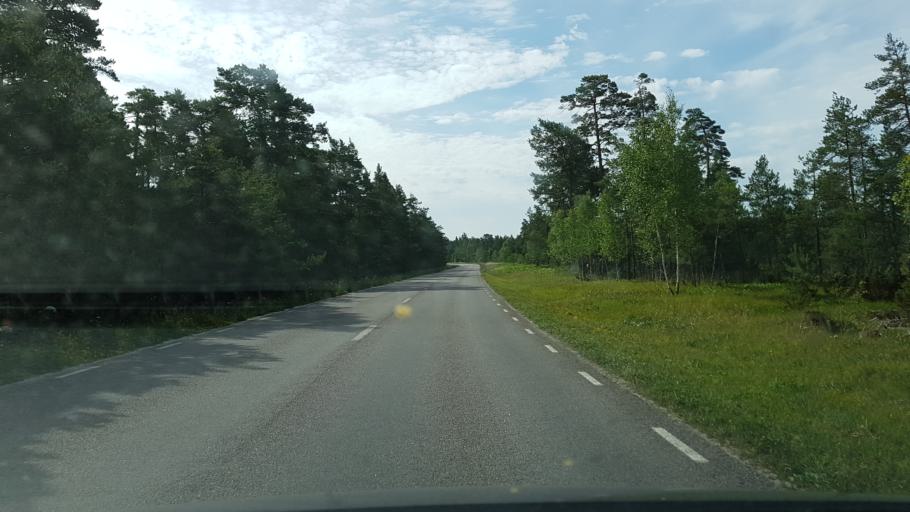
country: SE
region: Gotland
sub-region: Gotland
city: Hemse
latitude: 57.4565
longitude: 18.5774
